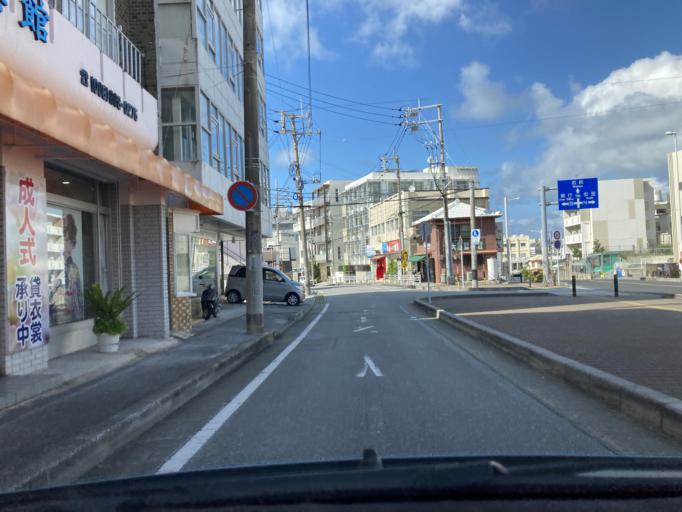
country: JP
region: Okinawa
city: Naha-shi
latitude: 26.2135
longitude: 127.6850
